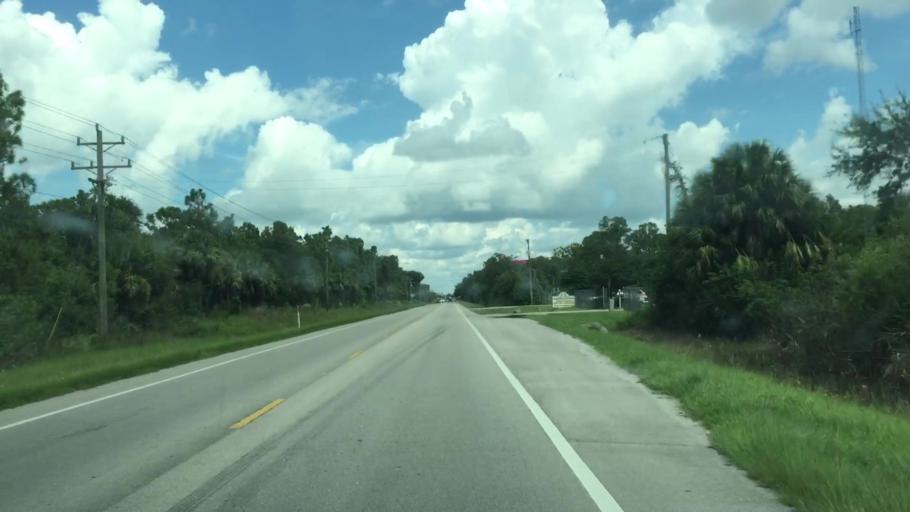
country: US
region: Florida
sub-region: Collier County
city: Immokalee
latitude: 26.3990
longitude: -81.4171
